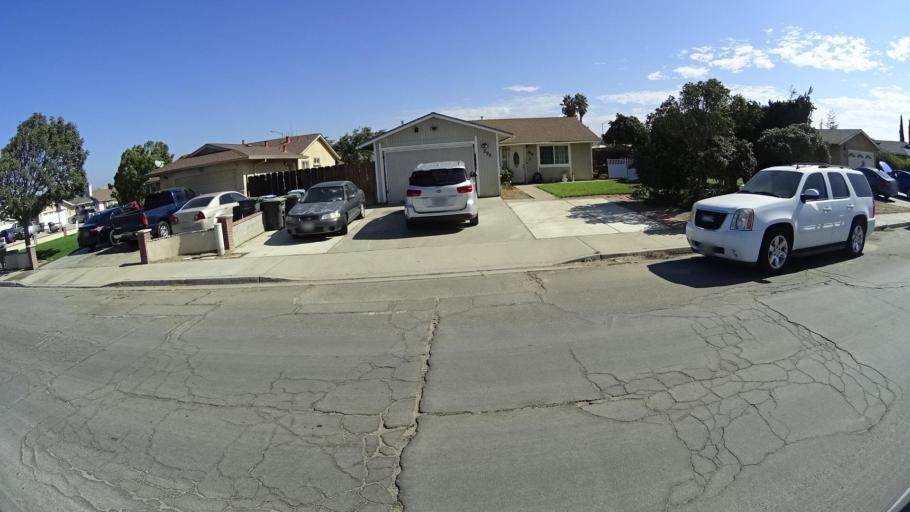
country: US
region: California
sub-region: Monterey County
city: Greenfield
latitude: 36.3194
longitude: -121.2532
